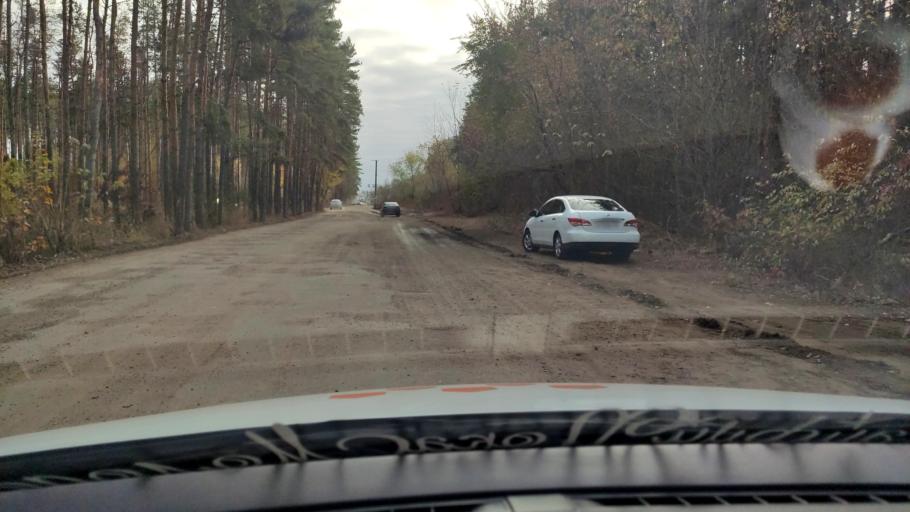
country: RU
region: Voronezj
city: Podgornoye
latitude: 51.7213
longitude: 39.1611
